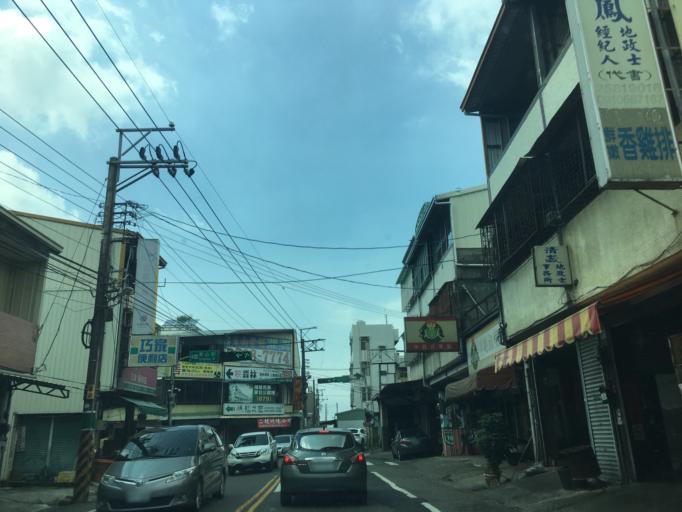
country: TW
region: Taiwan
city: Fengyuan
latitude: 24.2182
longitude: 120.7960
